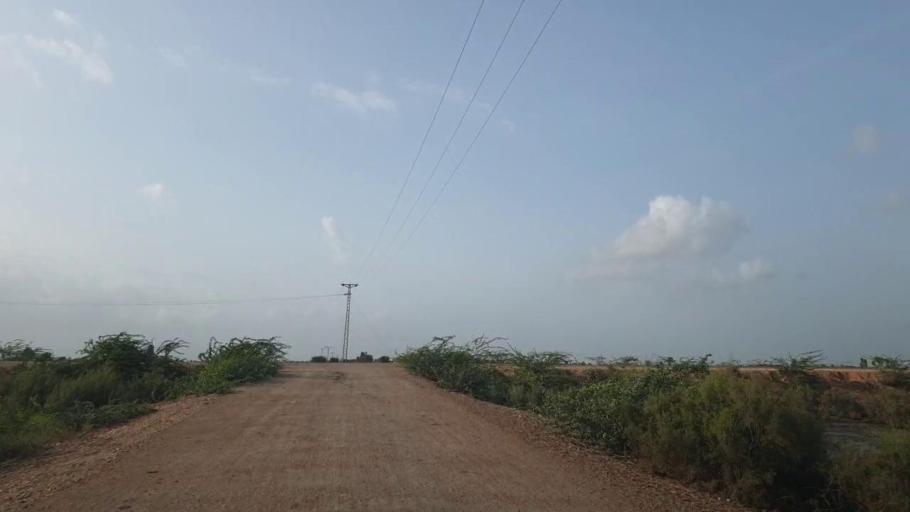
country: PK
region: Sindh
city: Tando Bago
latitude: 24.6556
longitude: 69.1119
